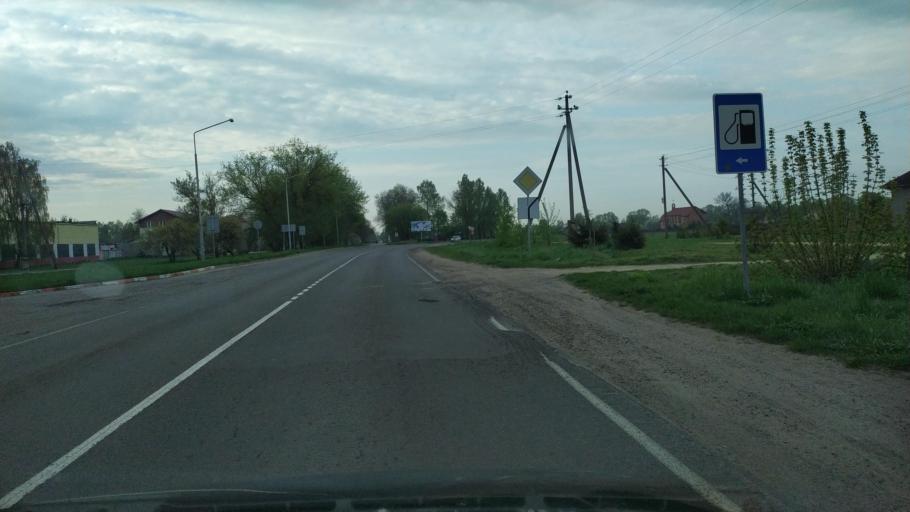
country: BY
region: Brest
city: Zhabinka
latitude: 52.2056
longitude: 24.0045
